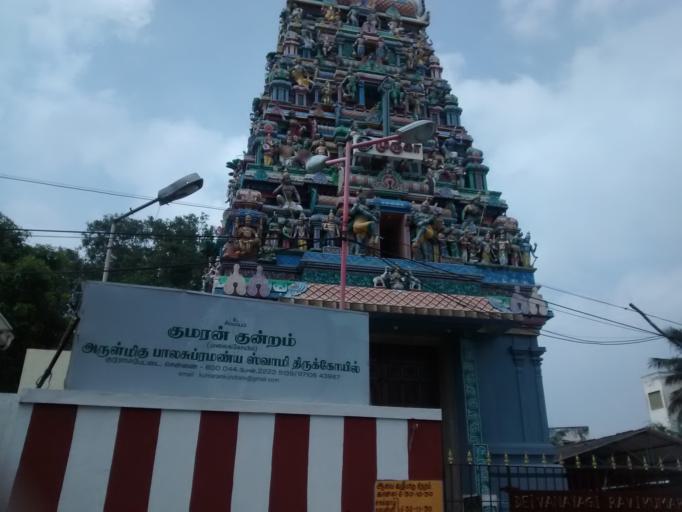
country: IN
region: Tamil Nadu
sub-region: Kancheepuram
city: Pallavaram
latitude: 12.9437
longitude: 80.1431
